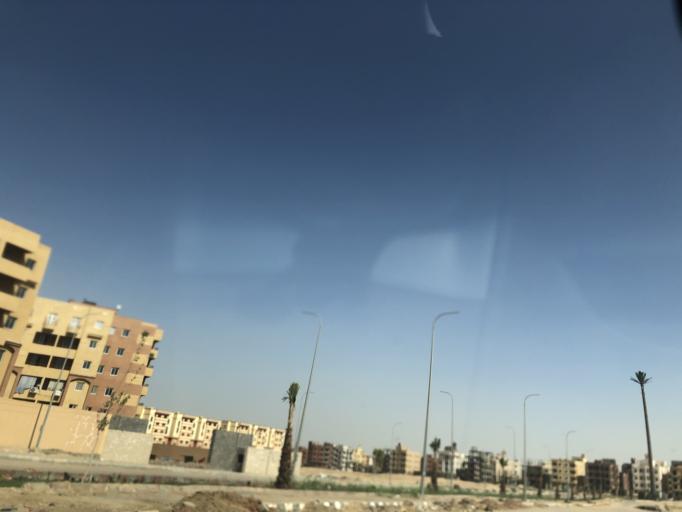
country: EG
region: Al Jizah
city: Madinat Sittah Uktubar
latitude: 29.9265
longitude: 31.0422
